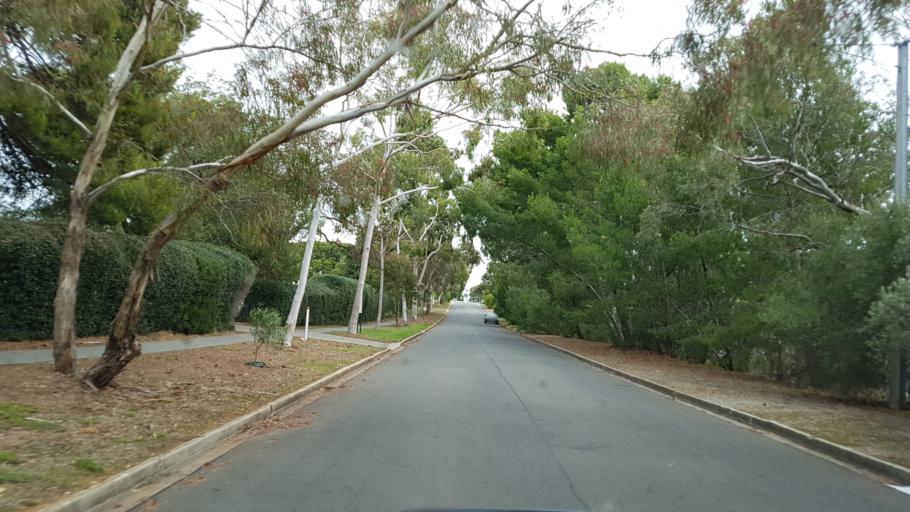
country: AU
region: South Australia
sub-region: Mitcham
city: Mitcham
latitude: -34.9833
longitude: 138.6218
